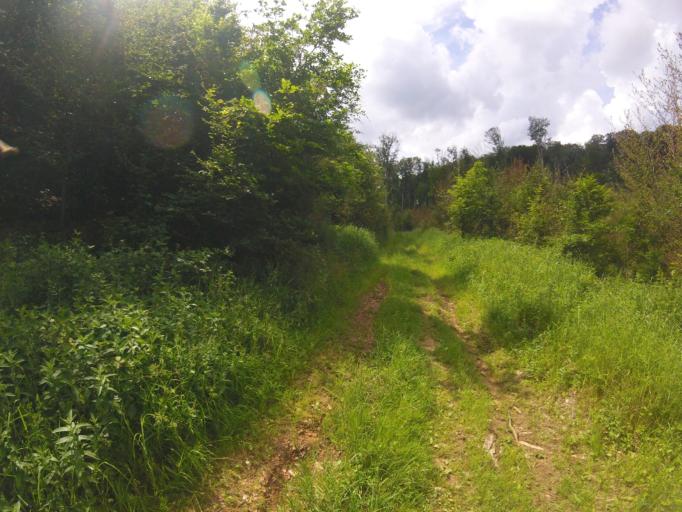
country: HU
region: Veszprem
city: Urkut
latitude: 47.1045
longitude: 17.6512
